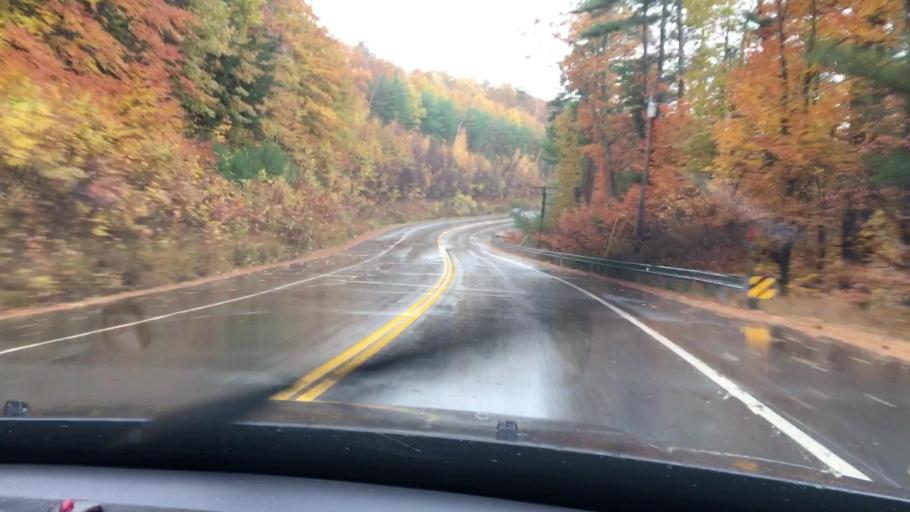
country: US
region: New Hampshire
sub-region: Grafton County
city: Holderness
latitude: 43.7319
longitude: -71.5710
